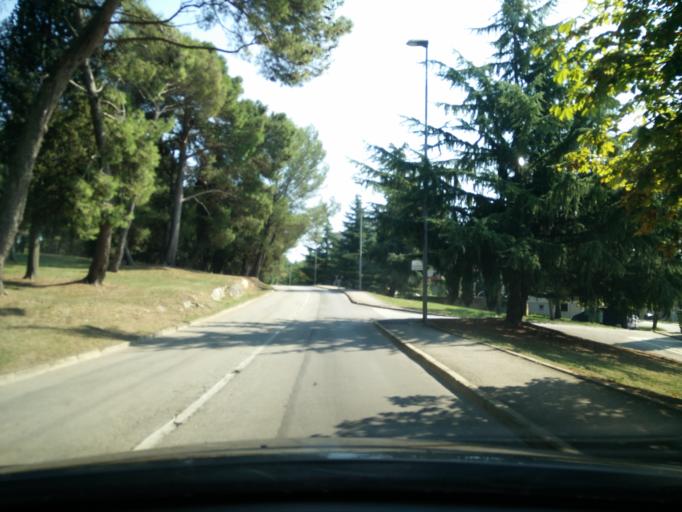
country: HR
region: Istarska
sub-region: Grad Porec
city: Porec
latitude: 45.2202
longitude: 13.5983
